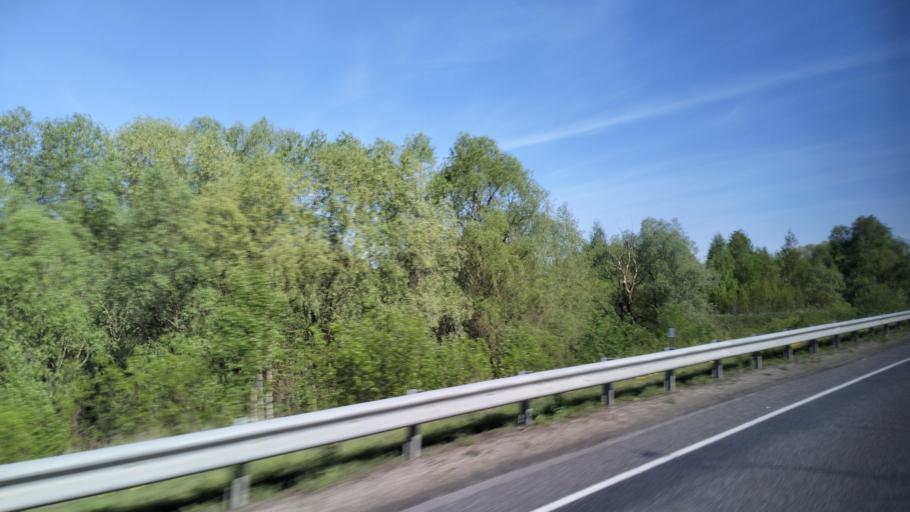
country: BY
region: Gomel
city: Turaw
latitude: 52.0928
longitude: 27.8292
